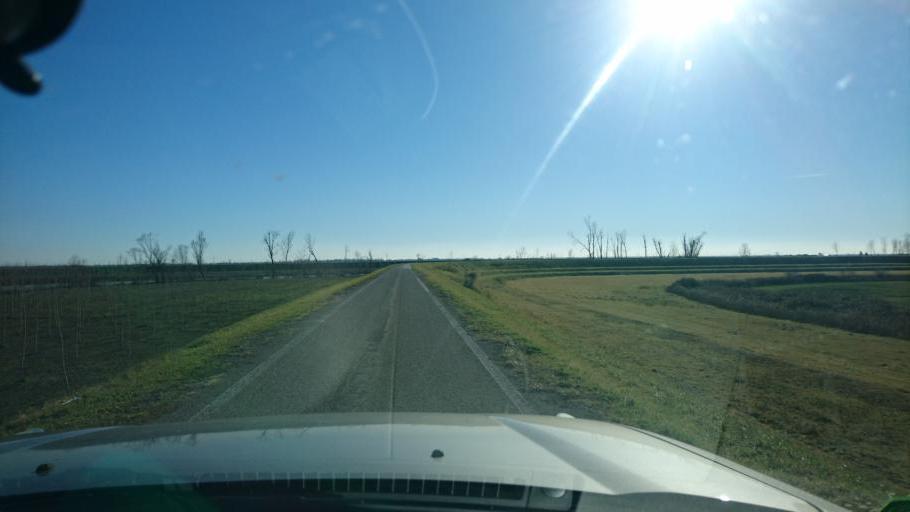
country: IT
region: Veneto
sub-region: Provincia di Rovigo
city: Ariano
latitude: 44.9337
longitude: 12.1577
